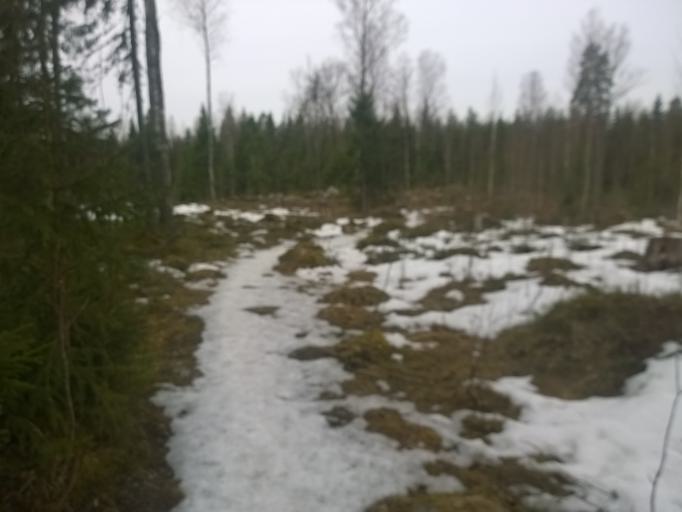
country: FI
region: Pirkanmaa
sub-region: Tampere
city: Tampere
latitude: 61.4479
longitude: 23.8242
